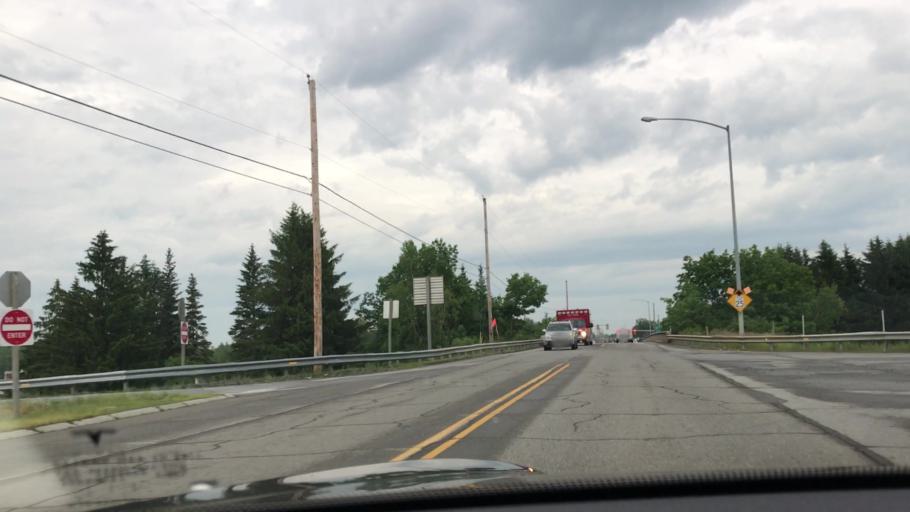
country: US
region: Maine
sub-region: Penobscot County
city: Orono
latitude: 44.9019
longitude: -68.6927
